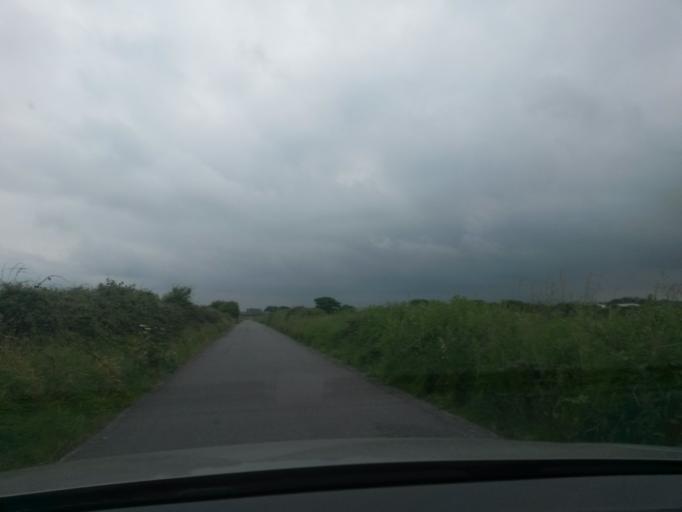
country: IE
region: Munster
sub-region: Ciarrai
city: Tralee
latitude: 52.3367
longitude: -9.7896
